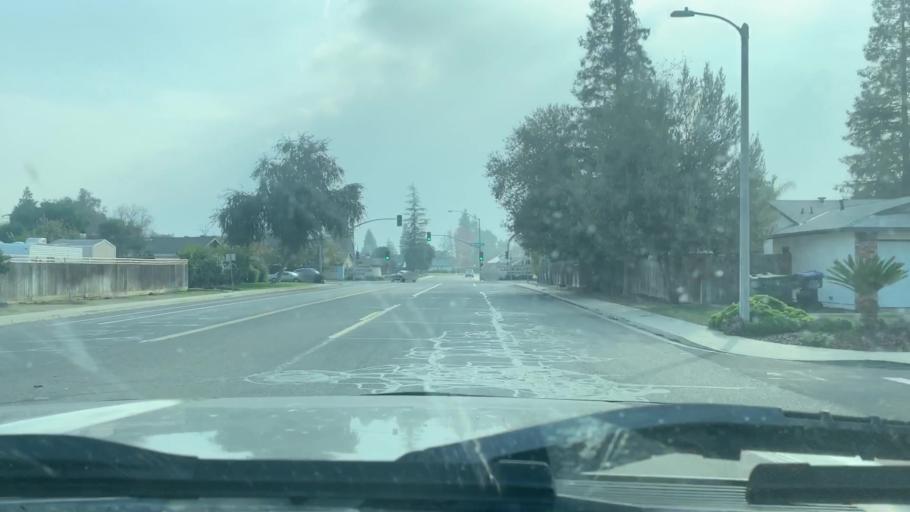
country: US
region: California
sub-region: Tulare County
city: Visalia
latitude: 36.3066
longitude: -119.3052
